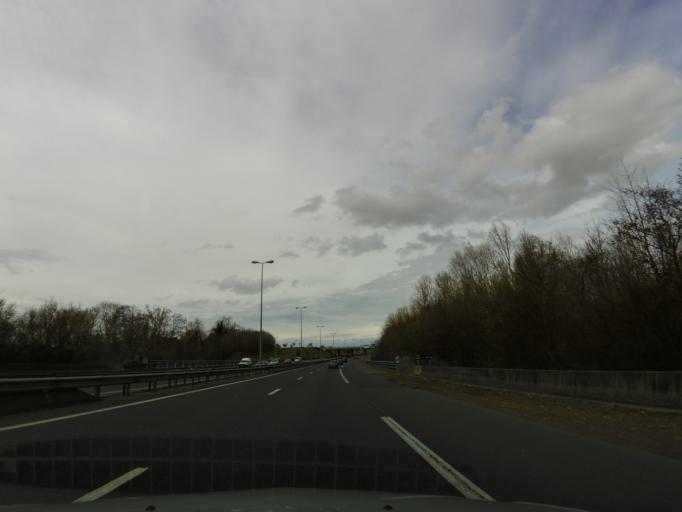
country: FR
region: Lower Normandy
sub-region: Departement du Calvados
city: Bretteville-sur-Odon
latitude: 49.1594
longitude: -0.4265
